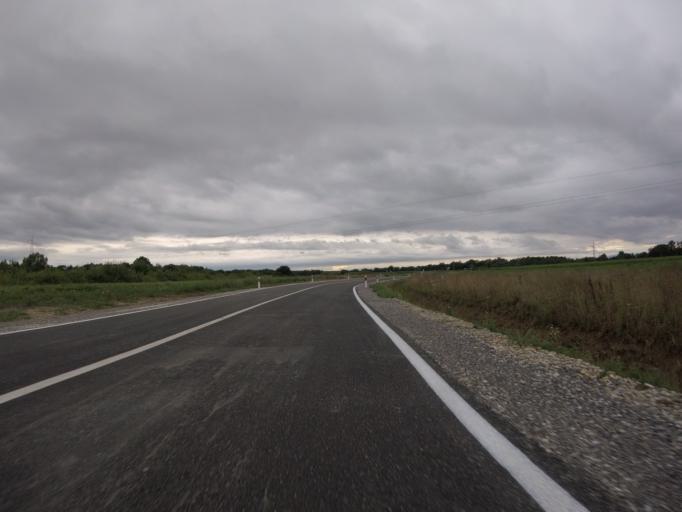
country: HR
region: Zagrebacka
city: Mraclin
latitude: 45.6572
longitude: 16.1024
